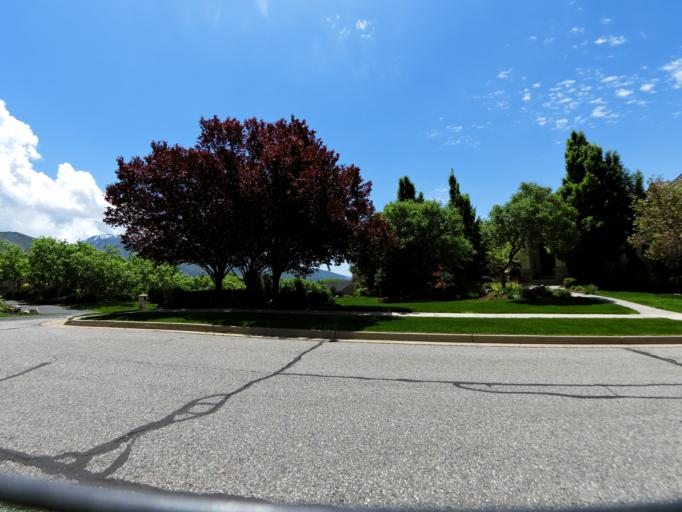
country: US
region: Utah
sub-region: Weber County
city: Uintah
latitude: 41.1620
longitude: -111.9214
